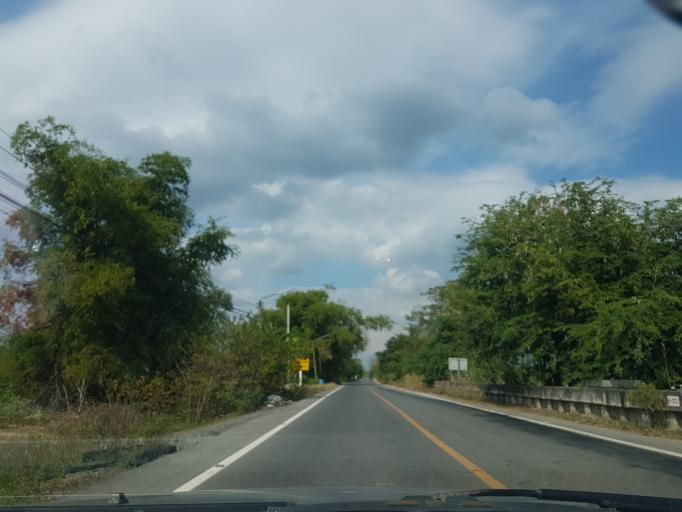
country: TH
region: Pathum Thani
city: Nong Suea
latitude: 14.1509
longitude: 100.8914
